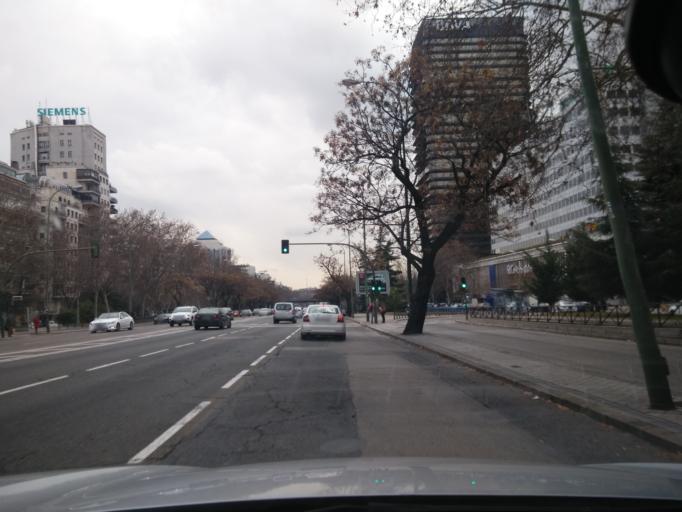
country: ES
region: Madrid
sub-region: Provincia de Madrid
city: Chamartin
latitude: 40.4497
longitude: -3.6910
